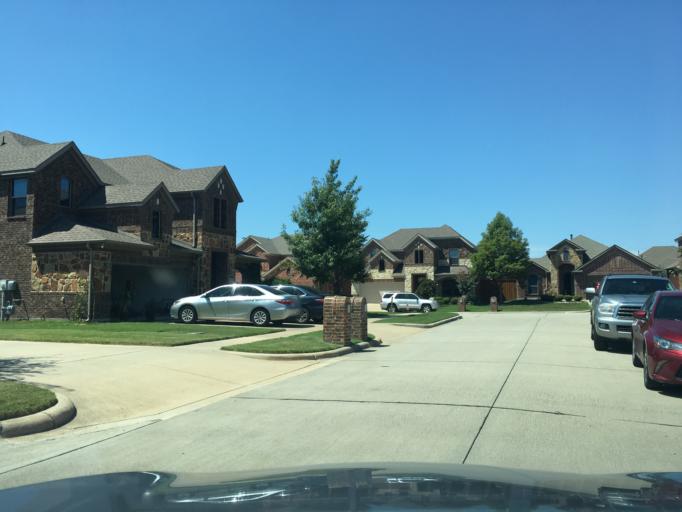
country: US
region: Texas
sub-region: Dallas County
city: Garland
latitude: 32.9552
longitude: -96.6345
